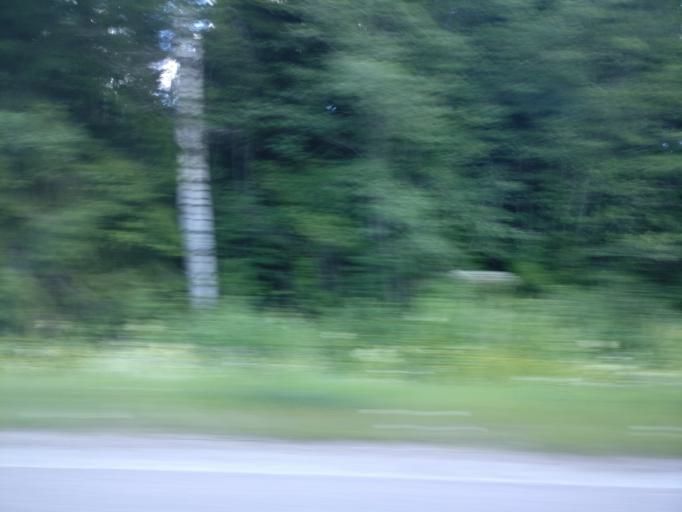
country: FI
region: Uusimaa
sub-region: Helsinki
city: Vihti
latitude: 60.4421
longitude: 24.4976
